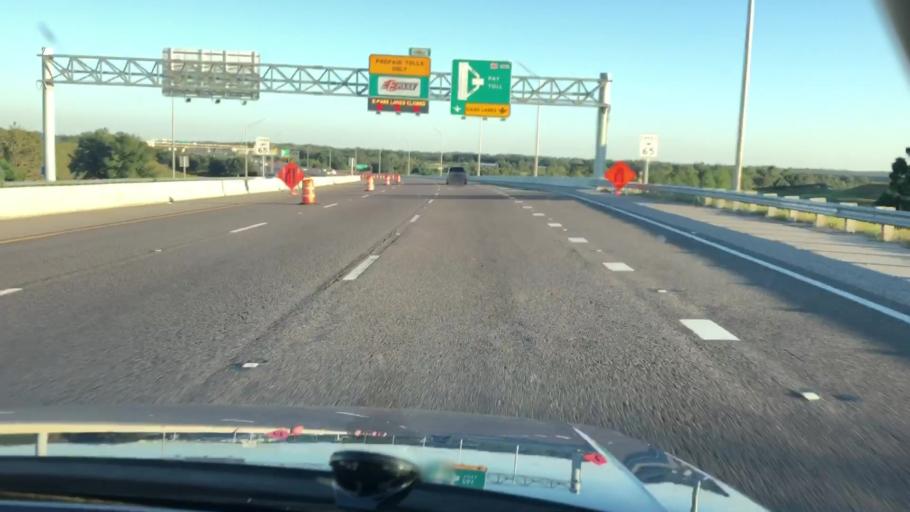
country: US
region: Florida
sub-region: Orange County
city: South Apopka
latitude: 28.6480
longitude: -81.5162
